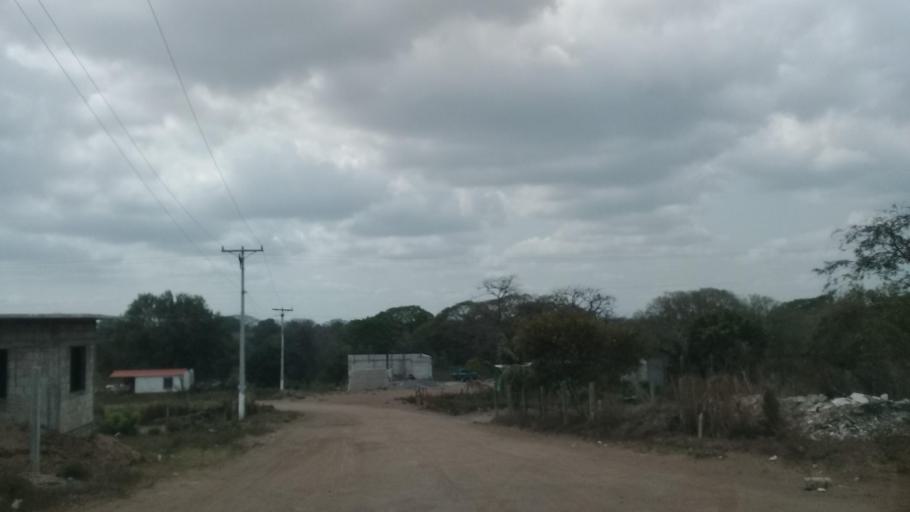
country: MX
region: Veracruz
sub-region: Veracruz
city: Las Amapolas
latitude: 19.1350
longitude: -96.2422
